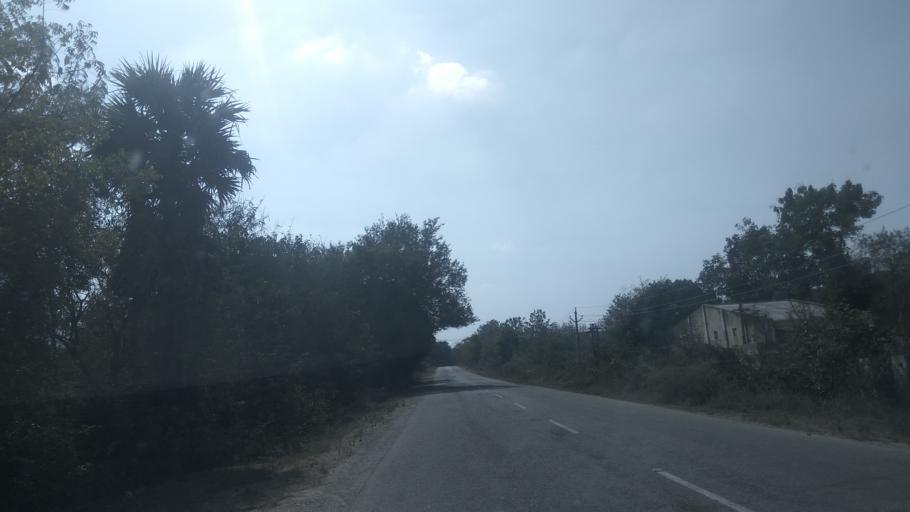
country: IN
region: Andhra Pradesh
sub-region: Chittoor
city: Renigunta
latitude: 13.5536
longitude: 79.4980
